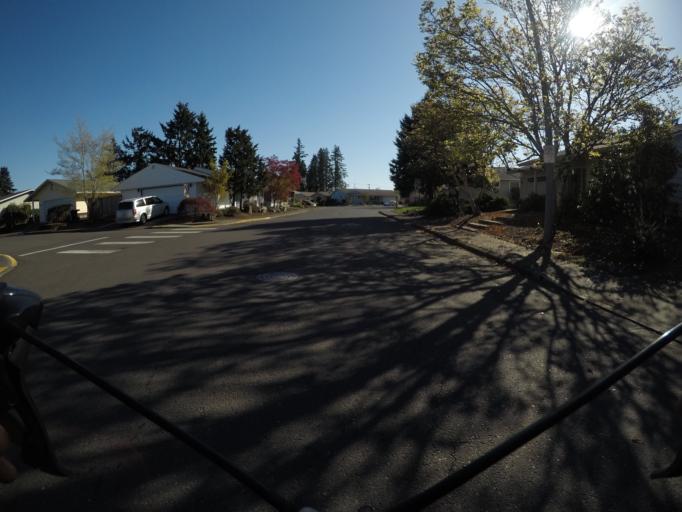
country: US
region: Oregon
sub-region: Washington County
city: King City
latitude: 45.3996
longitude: -122.8019
